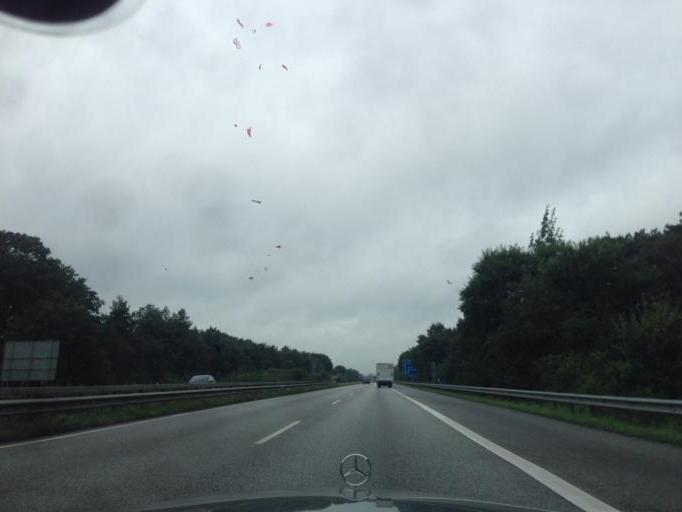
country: DE
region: Schleswig-Holstein
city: Eisendorf
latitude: 54.2090
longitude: 9.8680
